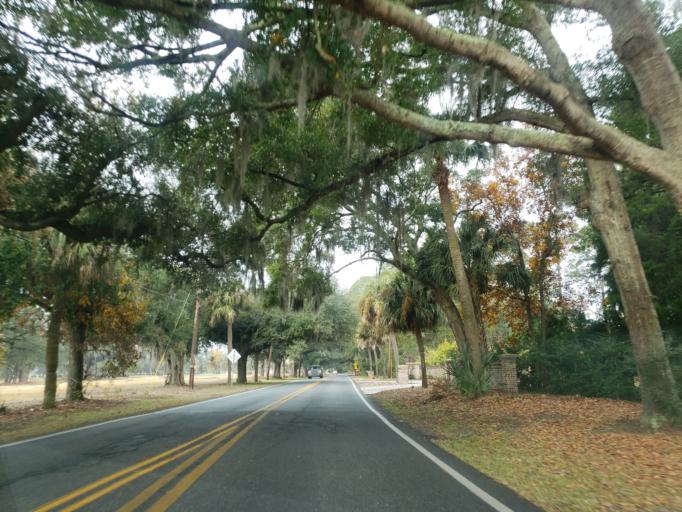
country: US
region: Georgia
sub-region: Chatham County
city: Wilmington Island
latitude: 32.0051
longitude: -80.9945
